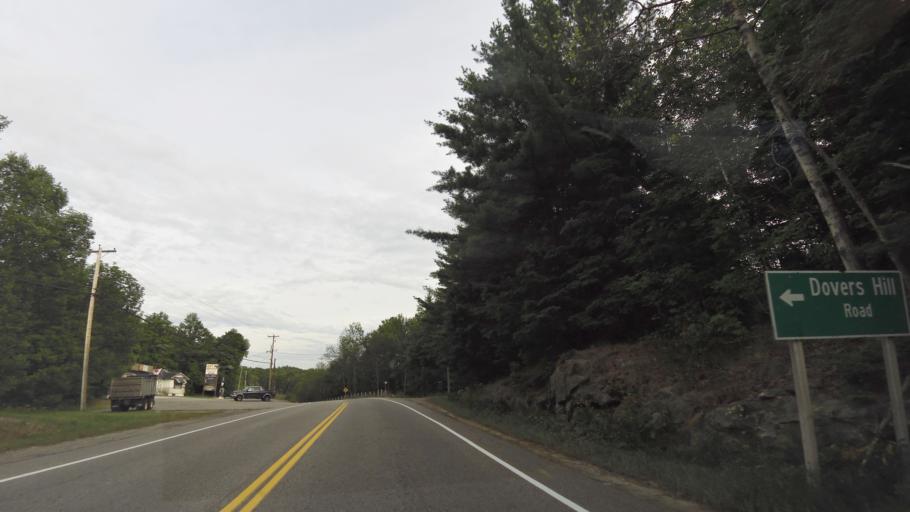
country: CA
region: Ontario
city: Bancroft
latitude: 45.0424
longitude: -78.4887
